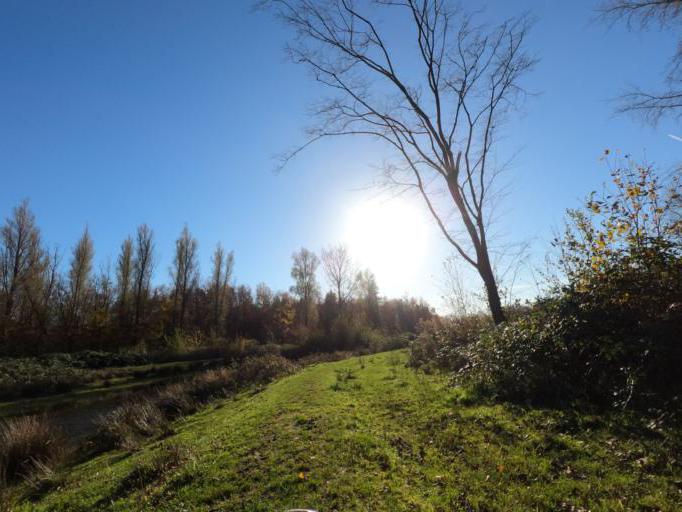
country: NL
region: Gelderland
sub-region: Gemeente Nijkerk
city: Nijkerk
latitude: 52.2663
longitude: 5.4429
